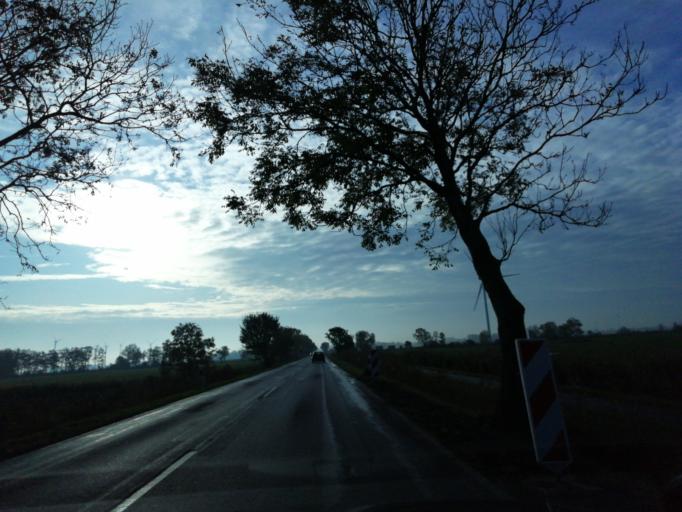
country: DE
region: Lower Saxony
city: Fedderwarden
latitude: 53.6134
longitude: 8.0402
